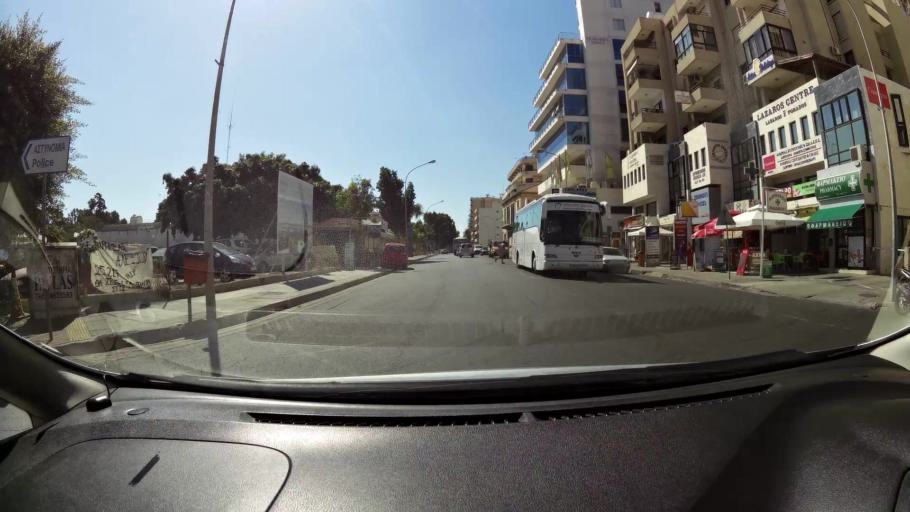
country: CY
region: Larnaka
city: Larnaca
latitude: 34.9189
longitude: 33.6366
